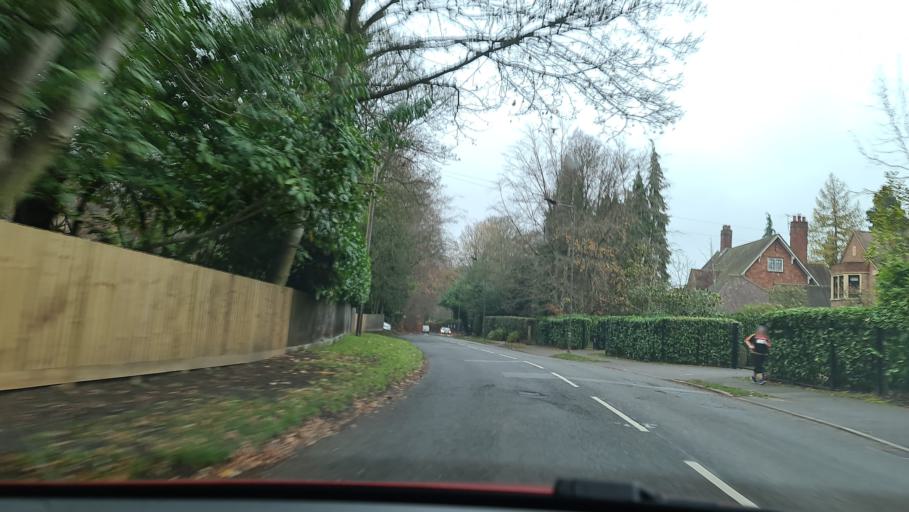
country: GB
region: England
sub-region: Buckinghamshire
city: Beaconsfield
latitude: 51.6158
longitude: -0.6375
